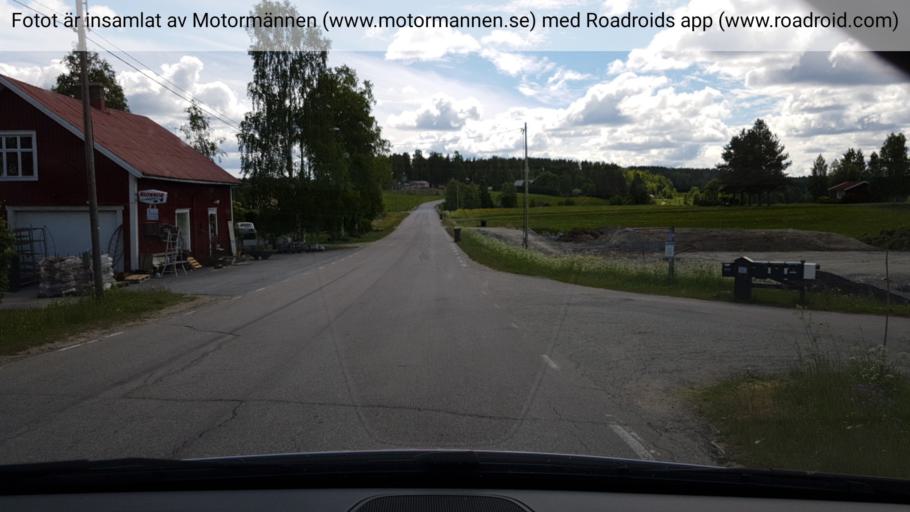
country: SE
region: Vaesterbotten
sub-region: Umea Kommun
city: Roback
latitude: 64.0377
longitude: 20.0767
